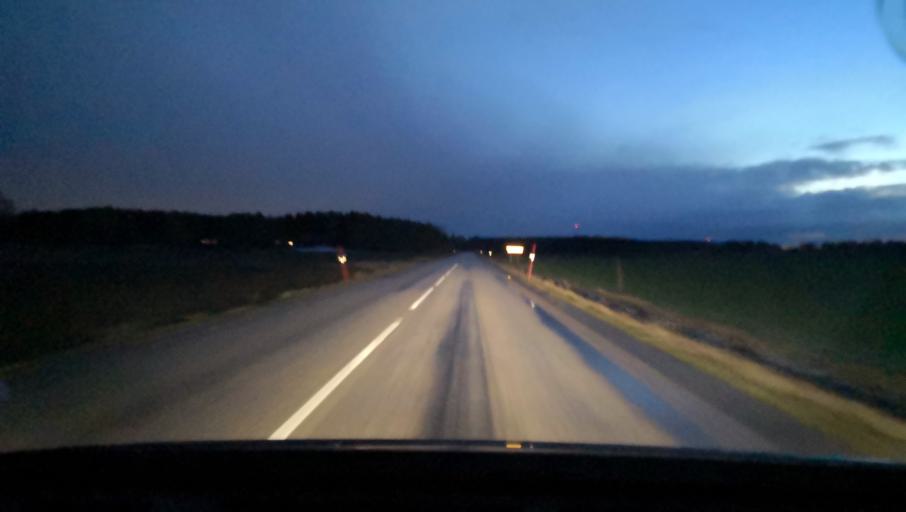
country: SE
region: Vaestmanland
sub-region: Vasteras
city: Skultuna
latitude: 59.7510
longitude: 16.4552
